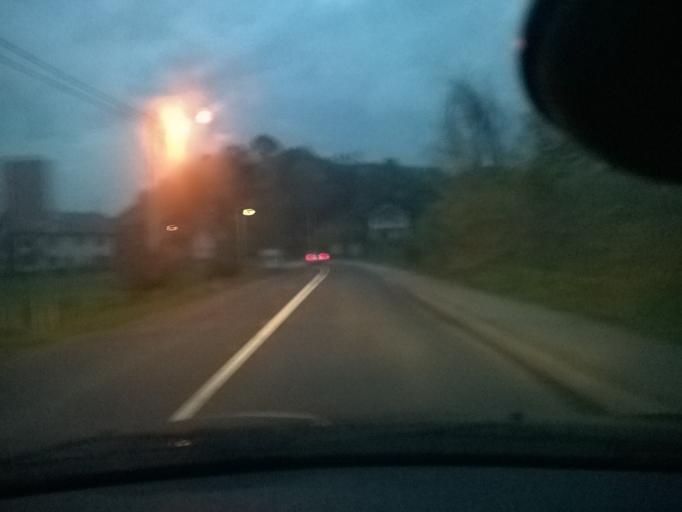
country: HR
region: Krapinsko-Zagorska
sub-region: Grad Krapina
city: Krapina
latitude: 46.0974
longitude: 15.9045
